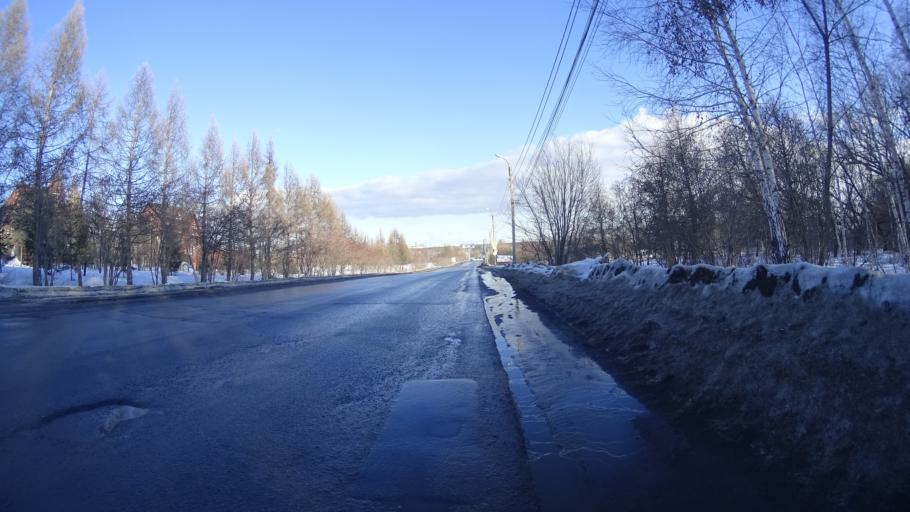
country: RU
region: Chelyabinsk
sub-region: Gorod Chelyabinsk
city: Chelyabinsk
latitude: 55.1489
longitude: 61.2956
